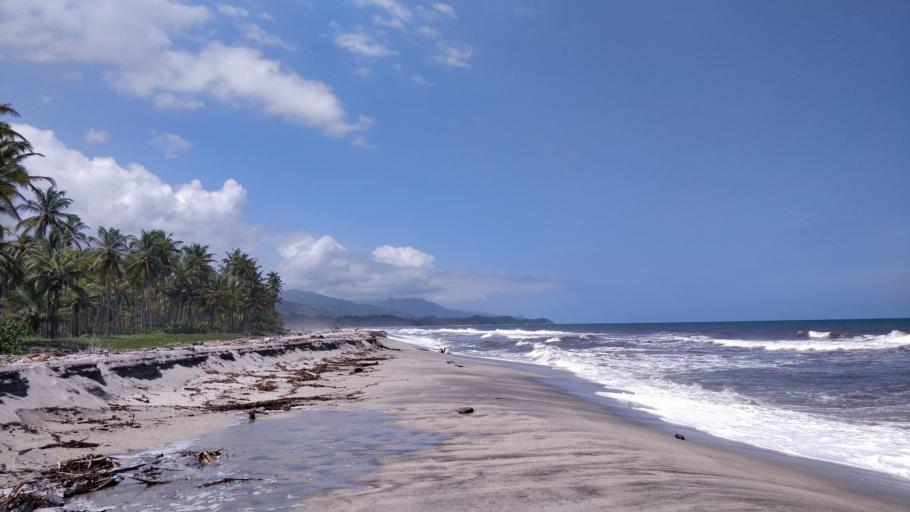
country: CO
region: Magdalena
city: Santa Marta
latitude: 11.2730
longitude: -73.8472
